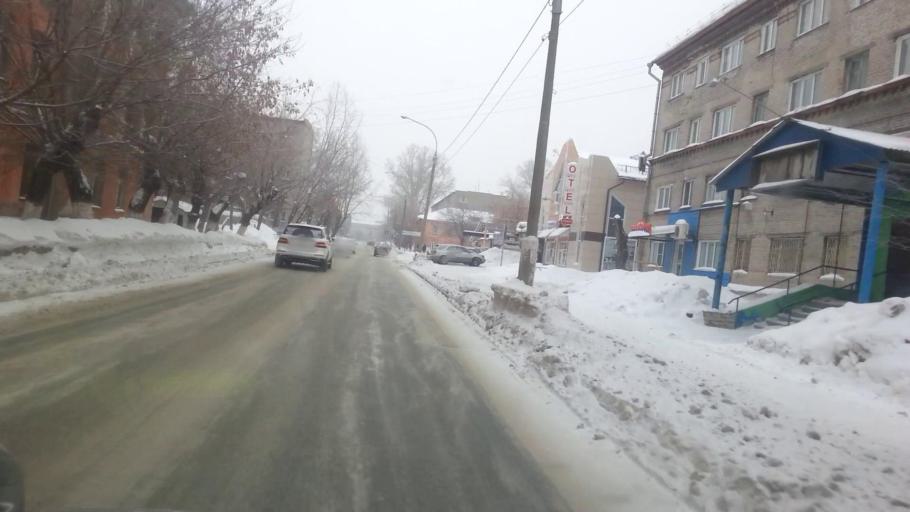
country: RU
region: Altai Krai
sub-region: Gorod Barnaulskiy
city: Barnaul
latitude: 53.3807
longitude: 83.7331
